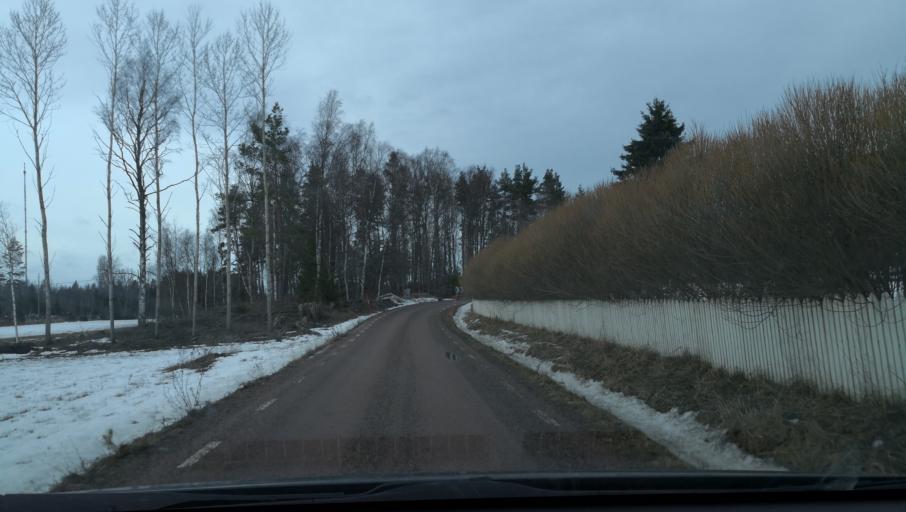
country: SE
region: Vaestmanland
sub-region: Vasteras
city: Skultuna
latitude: 59.6292
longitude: 16.4131
